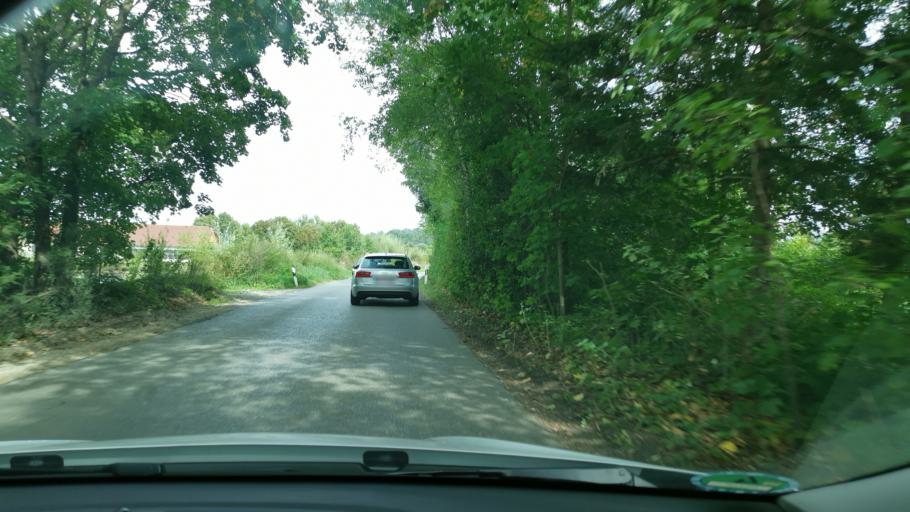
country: DE
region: Bavaria
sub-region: Upper Bavaria
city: Bergkirchen
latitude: 48.2468
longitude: 11.3597
